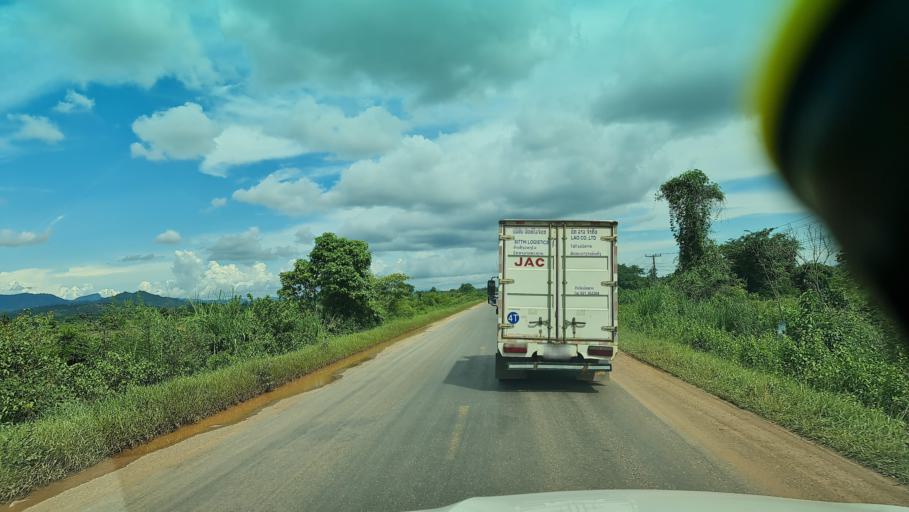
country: LA
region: Bolikhamxai
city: Ban Nahin
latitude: 18.1876
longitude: 104.2247
